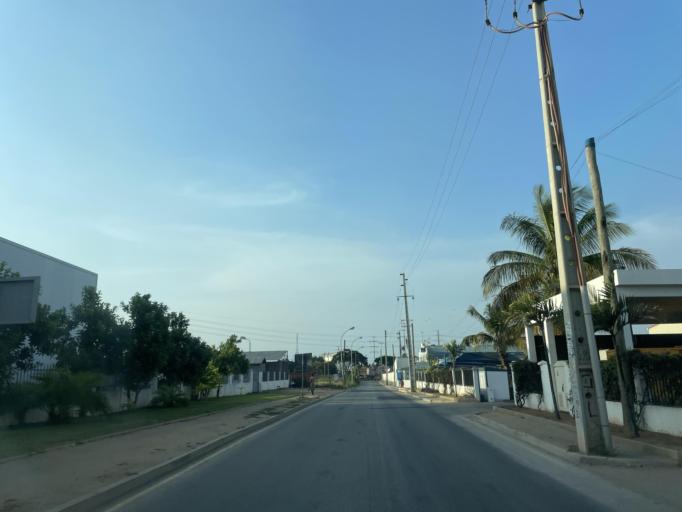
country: AO
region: Luanda
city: Luanda
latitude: -8.9080
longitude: 13.1841
